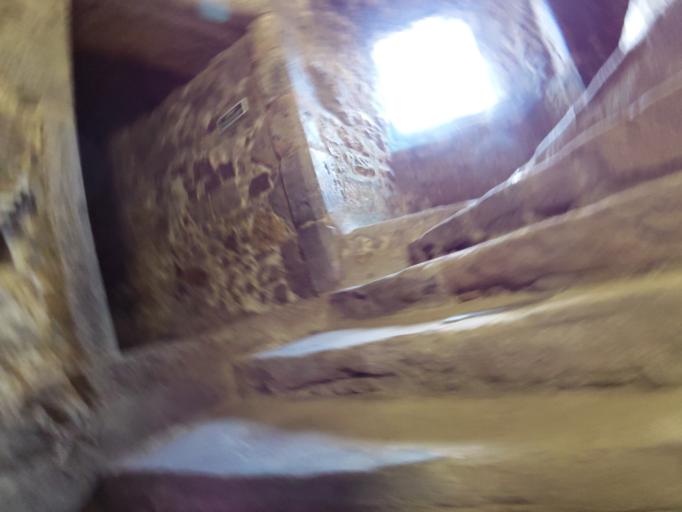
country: GB
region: Scotland
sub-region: West Lothian
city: Seafield
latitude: 55.9250
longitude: -3.1409
